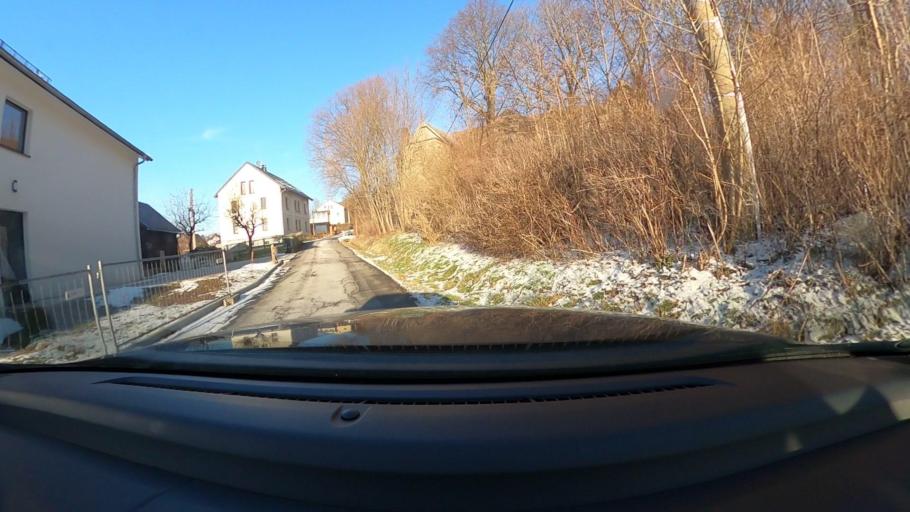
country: DE
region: Saxony
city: Frankenstein
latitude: 50.9389
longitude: 13.2175
